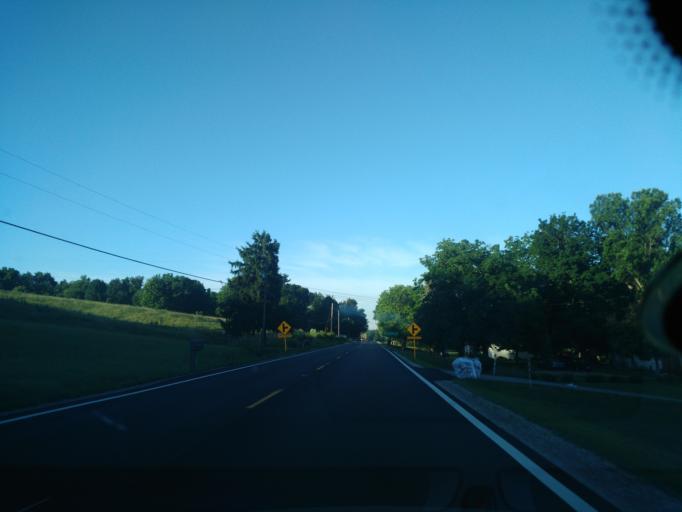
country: US
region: Ohio
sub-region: Ross County
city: Kingston
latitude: 39.4378
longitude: -82.9485
